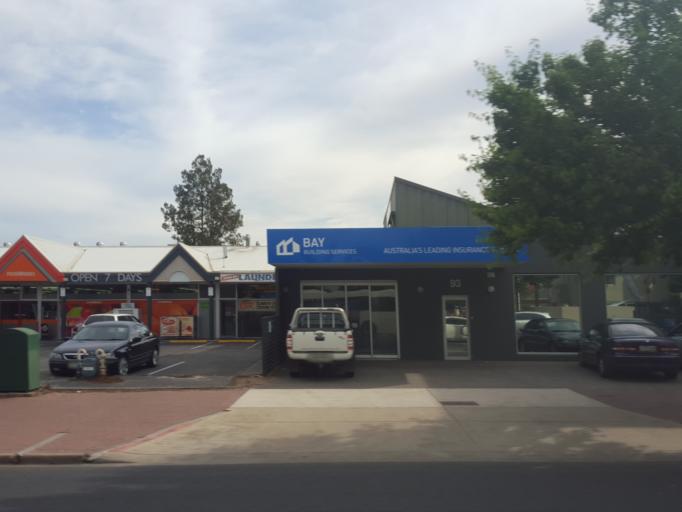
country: AU
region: South Australia
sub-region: Adelaide
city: North Adelaide
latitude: -34.8941
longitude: 138.5795
